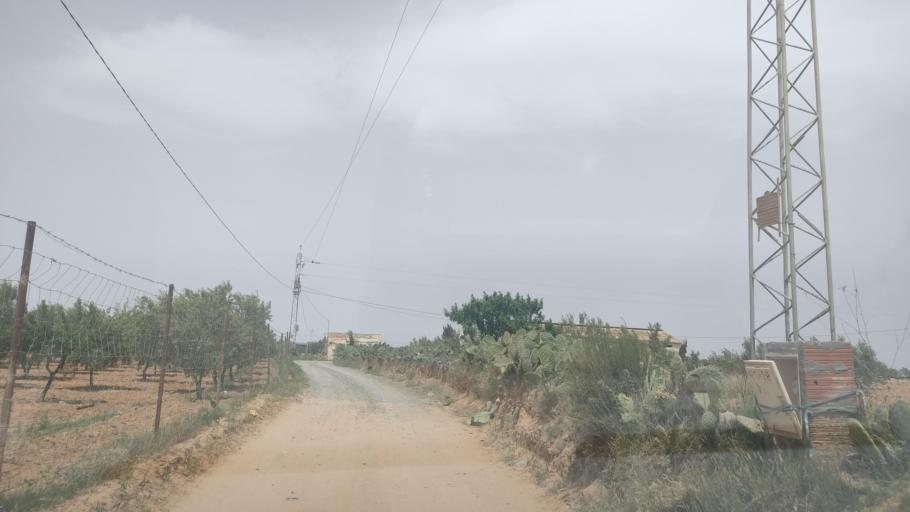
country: TN
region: Safaqis
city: Sfax
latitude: 34.8390
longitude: 10.5956
